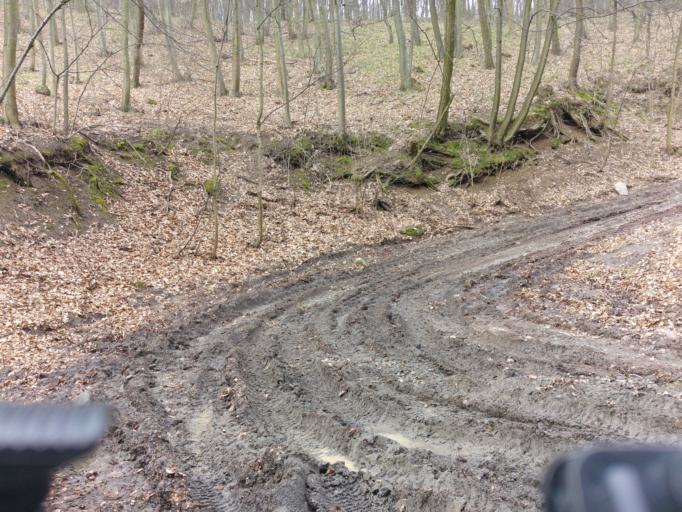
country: HU
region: Pest
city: Dunabogdany
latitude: 47.7557
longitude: 19.0271
